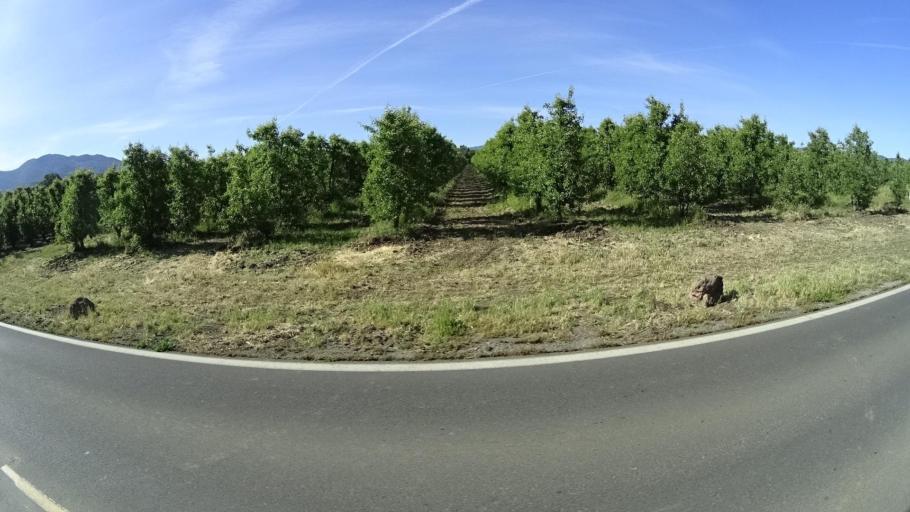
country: US
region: California
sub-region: Lake County
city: Kelseyville
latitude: 39.0112
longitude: -122.8414
